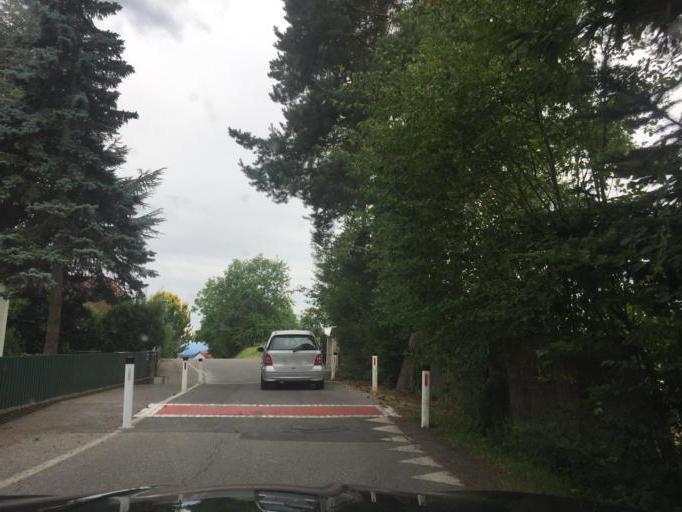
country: AT
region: Styria
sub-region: Politischer Bezirk Graz-Umgebung
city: Hart bei Graz
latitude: 47.0614
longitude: 15.5150
